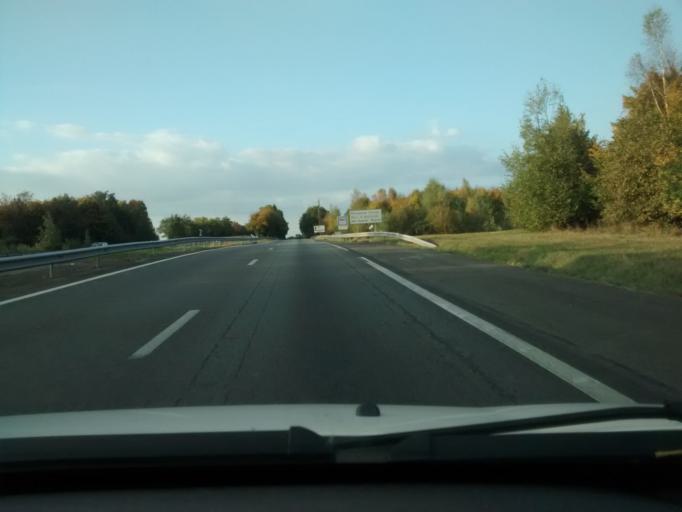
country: FR
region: Brittany
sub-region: Departement d'Ille-et-Vilaine
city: Grand-Fougeray
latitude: 47.7226
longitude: -1.7104
